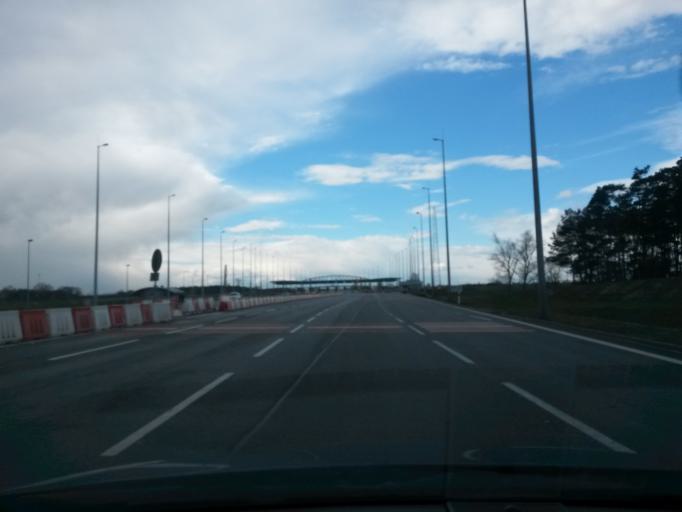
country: PL
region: Greater Poland Voivodeship
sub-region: Powiat slupecki
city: Ladek
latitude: 52.2207
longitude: 17.9556
